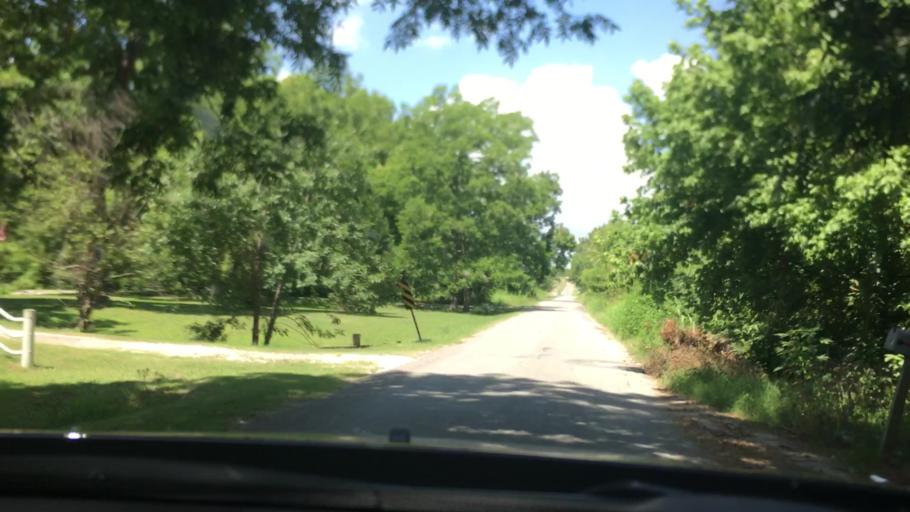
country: US
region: Oklahoma
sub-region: Pontotoc County
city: Ada
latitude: 34.6945
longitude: -96.5788
